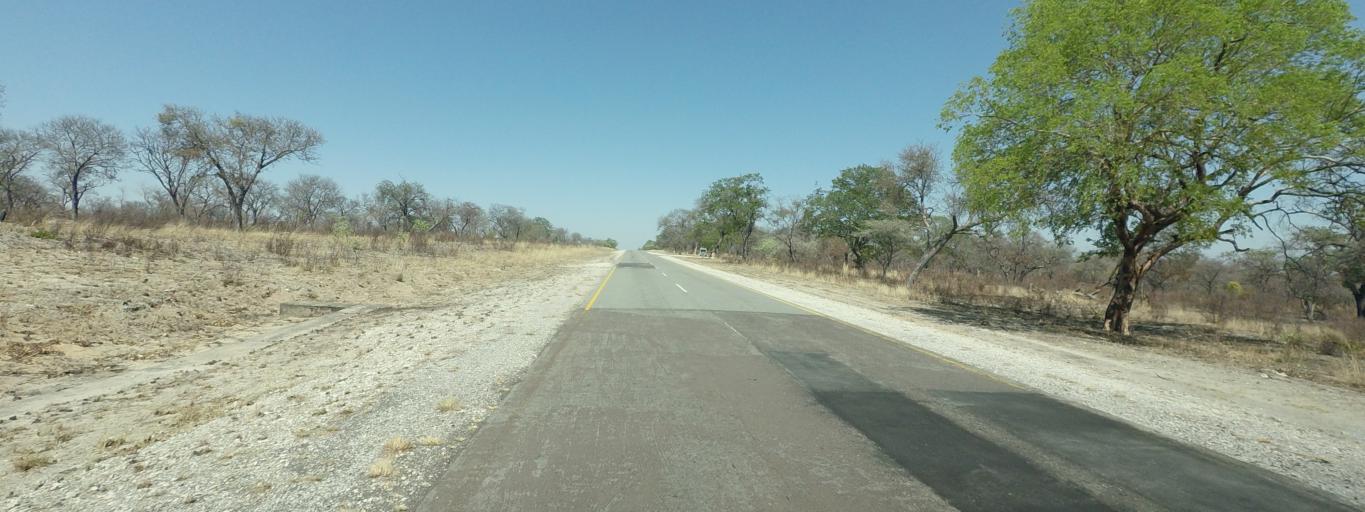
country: BW
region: North West
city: Shakawe
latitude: -17.9509
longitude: 22.5873
